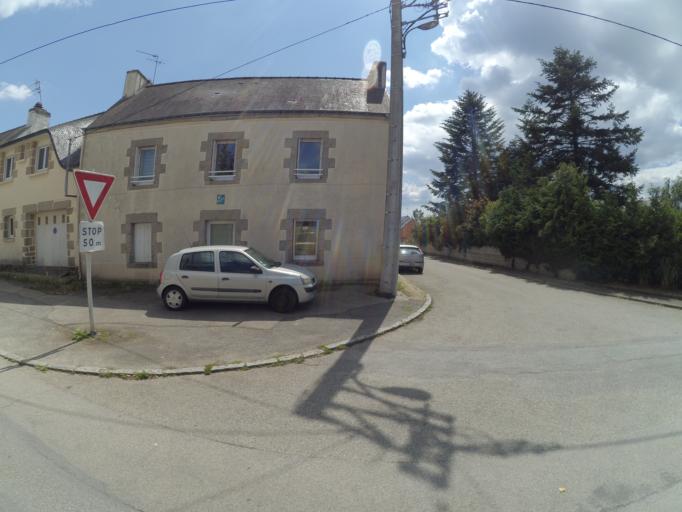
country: FR
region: Brittany
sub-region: Departement du Morbihan
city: Landaul
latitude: 47.7482
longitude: -3.0767
